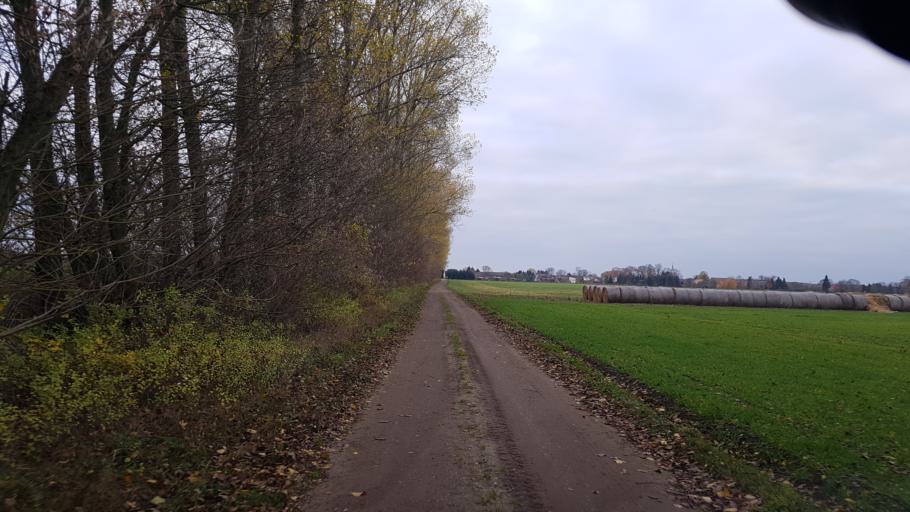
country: DE
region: Brandenburg
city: Sallgast
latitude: 51.6118
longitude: 13.8710
